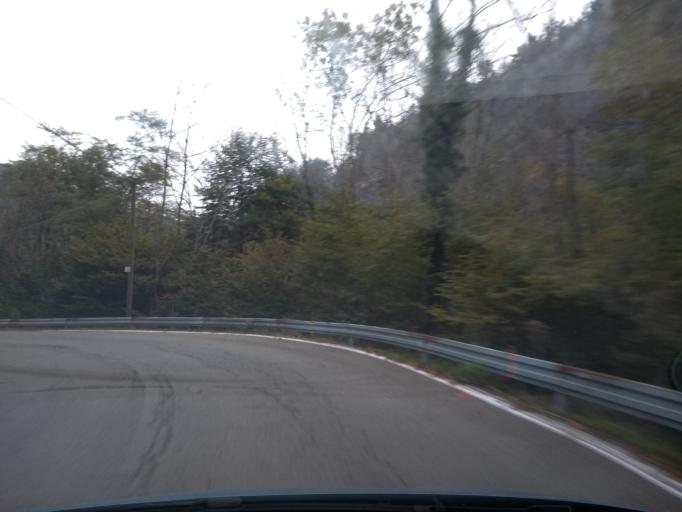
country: IT
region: Piedmont
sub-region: Provincia di Torino
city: Coassolo Torinese
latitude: 45.2952
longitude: 7.4566
